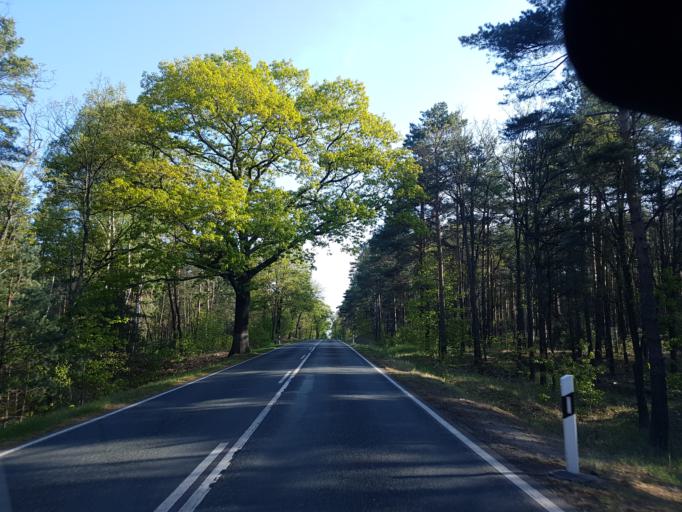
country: DE
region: Brandenburg
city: Altdobern
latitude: 51.6246
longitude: 14.0265
